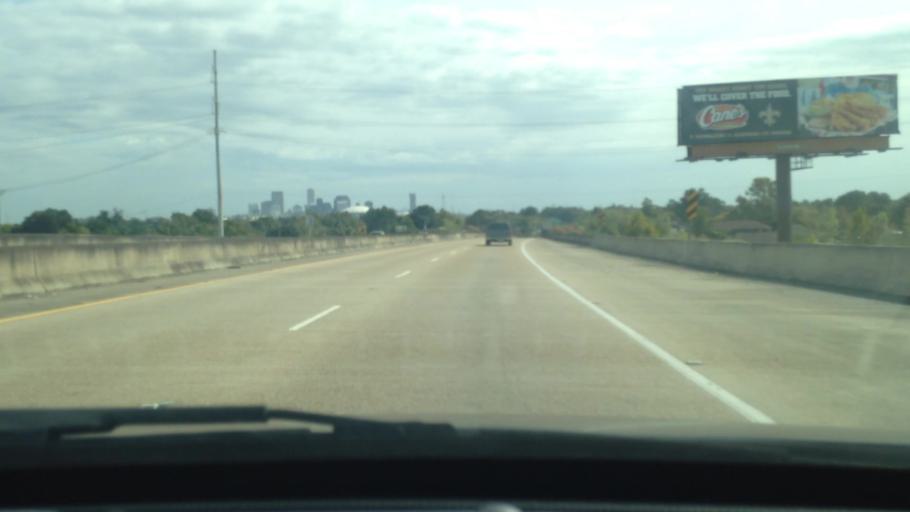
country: US
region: Louisiana
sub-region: Jefferson Parish
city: Jefferson
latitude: 29.9682
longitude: -90.1300
